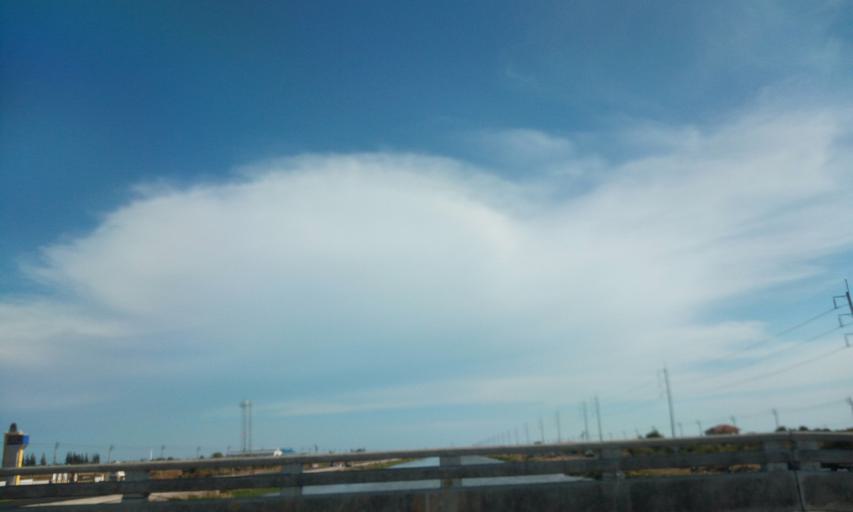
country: TH
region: Samut Prakan
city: Bang Bo District
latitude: 13.5270
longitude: 100.7485
